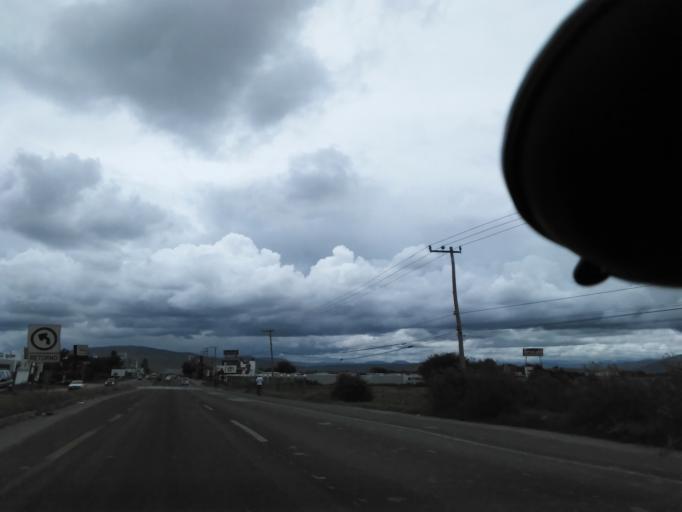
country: MX
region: Hidalgo
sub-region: Tula de Allende
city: Residencial Arboledas
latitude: 20.0591
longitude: -99.2913
